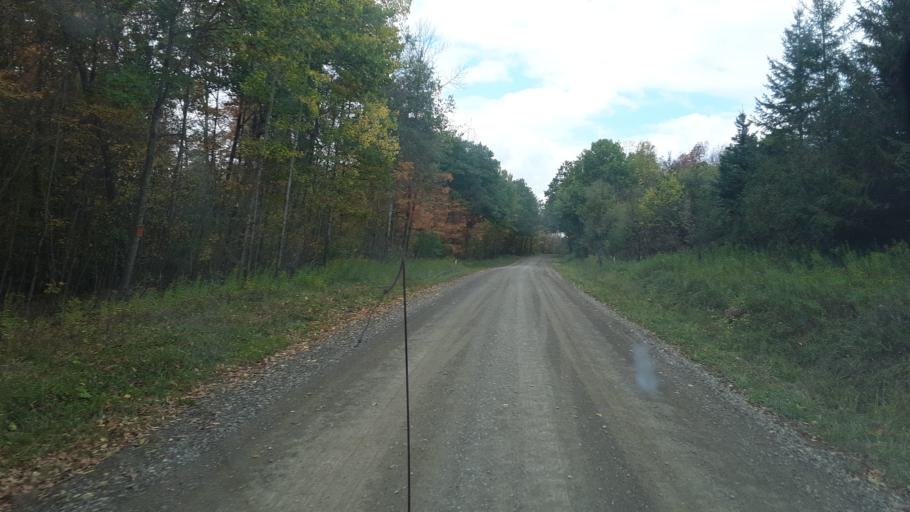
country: US
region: New York
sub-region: Allegany County
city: Alfred
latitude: 42.3813
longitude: -77.8575
